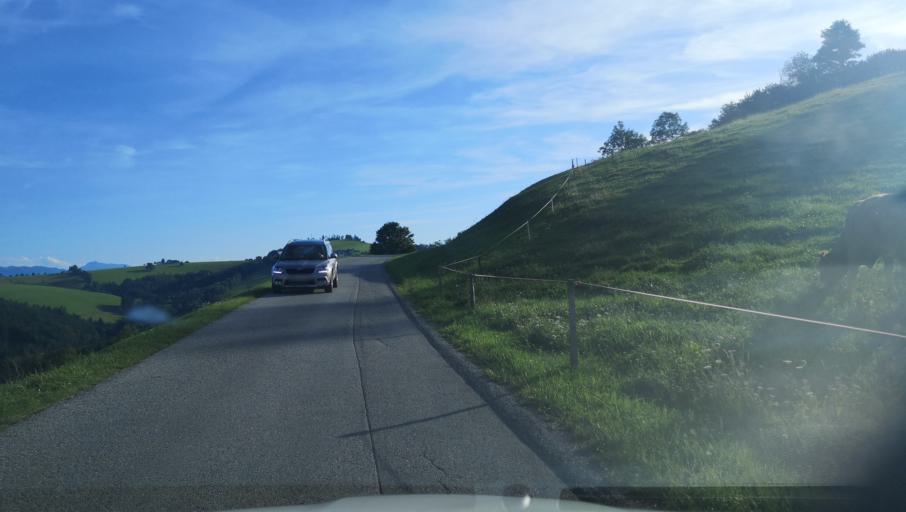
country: AT
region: Lower Austria
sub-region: Politischer Bezirk Amstetten
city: Neuhofen an der Ybbs
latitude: 48.0087
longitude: 14.8882
